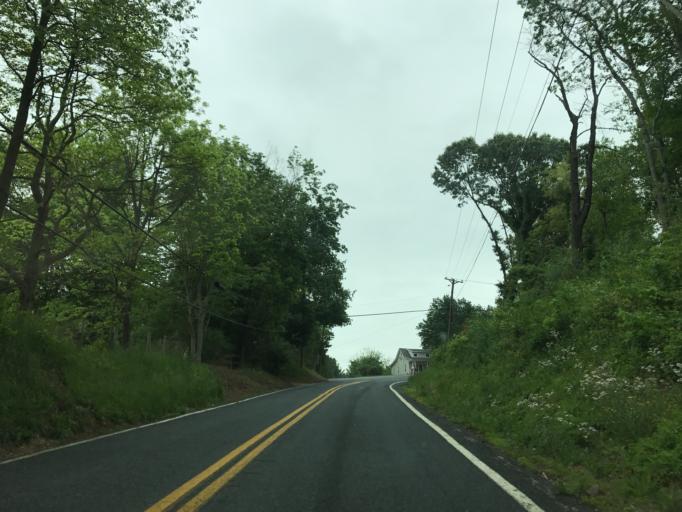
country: US
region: Pennsylvania
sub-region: York County
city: New Freedom
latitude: 39.6928
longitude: -76.7088
